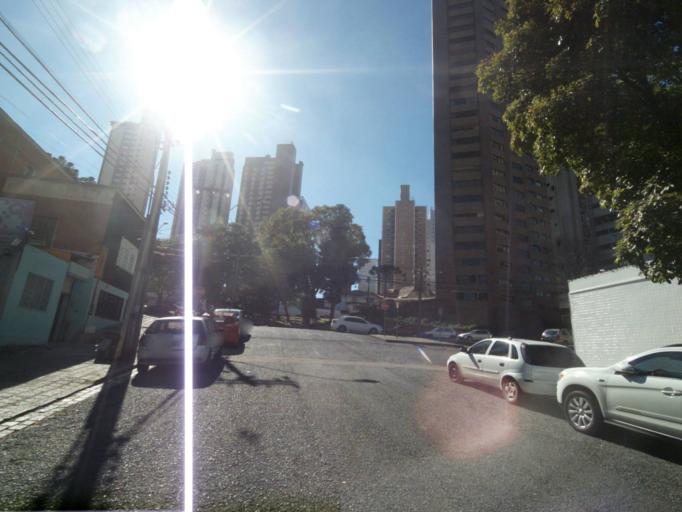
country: BR
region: Parana
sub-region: Curitiba
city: Curitiba
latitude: -25.4126
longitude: -49.2570
